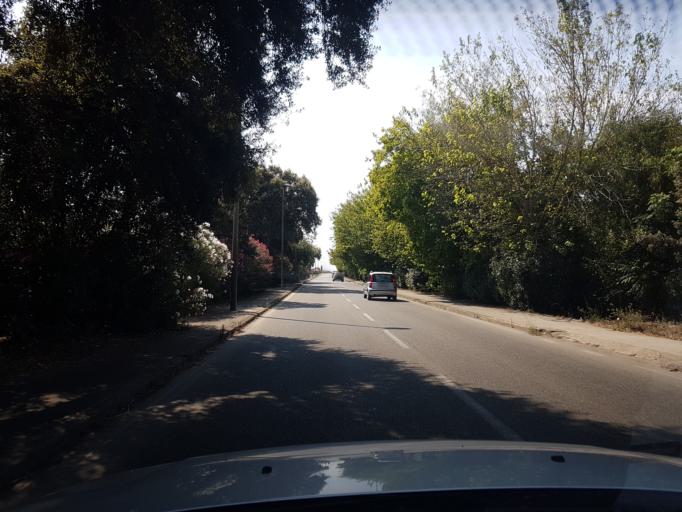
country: IT
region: Sardinia
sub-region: Provincia di Oristano
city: Donigala Fenugheddu
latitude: 39.9241
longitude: 8.5804
